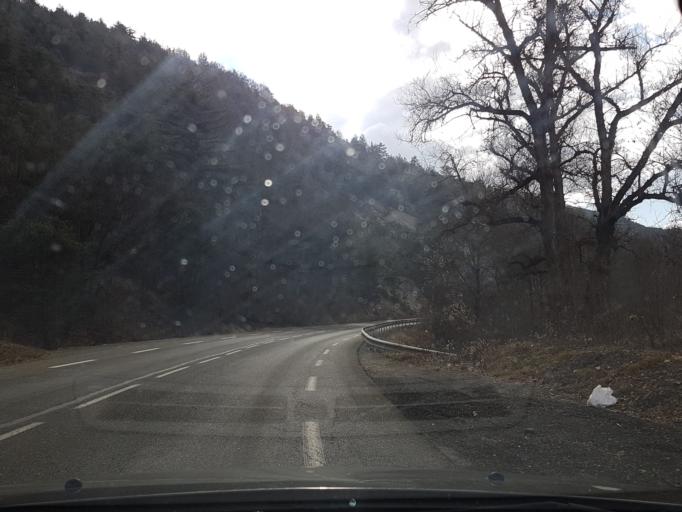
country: FR
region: Provence-Alpes-Cote d'Azur
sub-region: Departement des Hautes-Alpes
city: Gap
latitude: 44.5166
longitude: 6.0652
